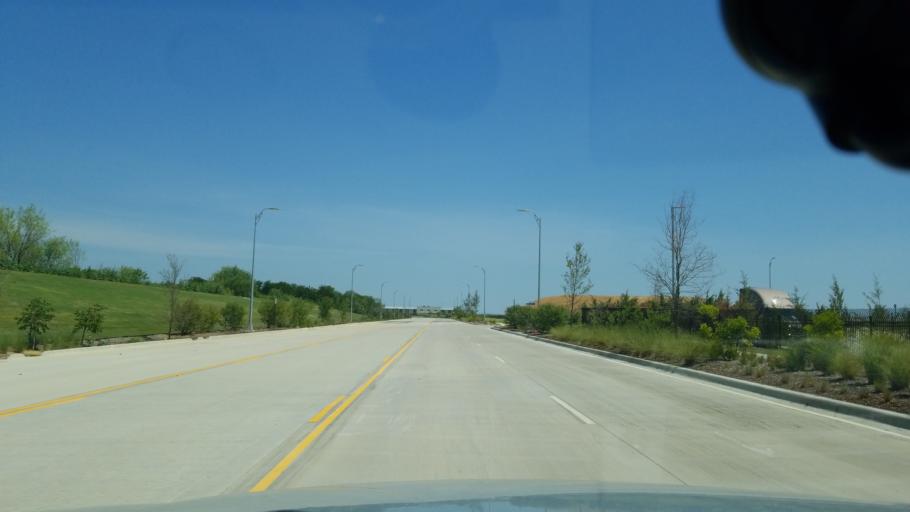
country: US
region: Texas
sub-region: Tarrant County
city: Euless
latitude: 32.8447
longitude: -97.0309
